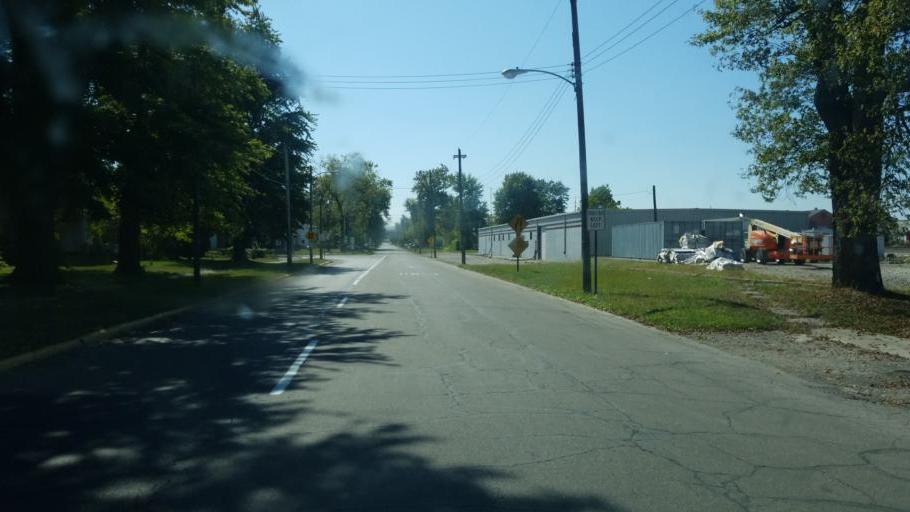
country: US
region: Ohio
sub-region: Marion County
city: Marion
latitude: 40.5880
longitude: -83.1395
